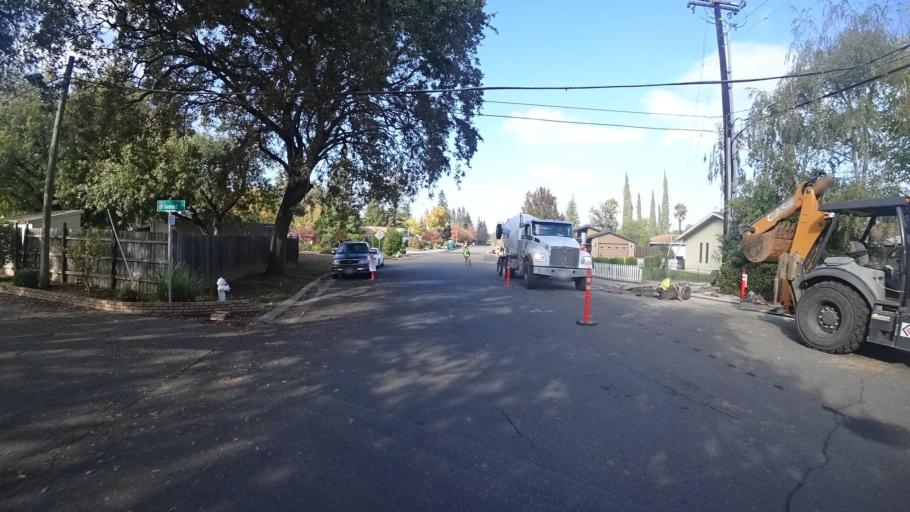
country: US
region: California
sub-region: Sacramento County
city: Elk Grove
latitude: 38.4111
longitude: -121.3624
